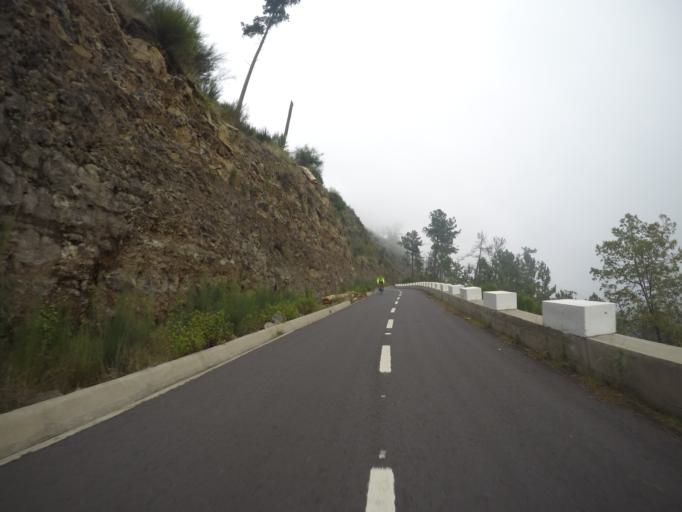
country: PT
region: Madeira
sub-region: Camara de Lobos
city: Curral das Freiras
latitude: 32.7038
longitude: -16.9567
